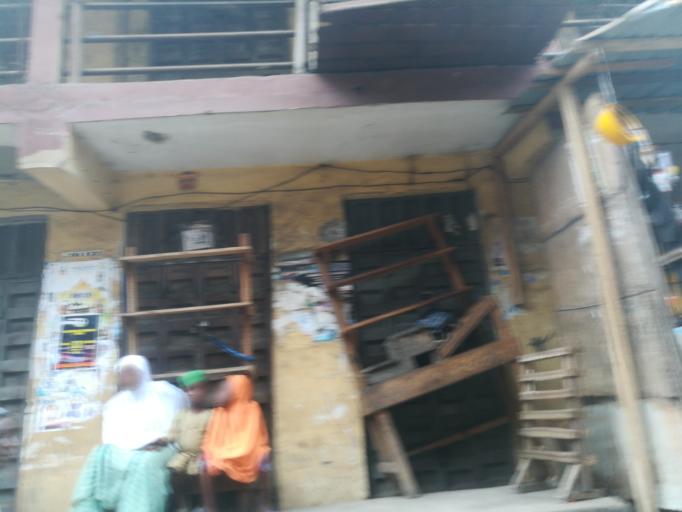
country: NG
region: Lagos
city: Lagos
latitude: 6.4585
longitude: 3.3885
